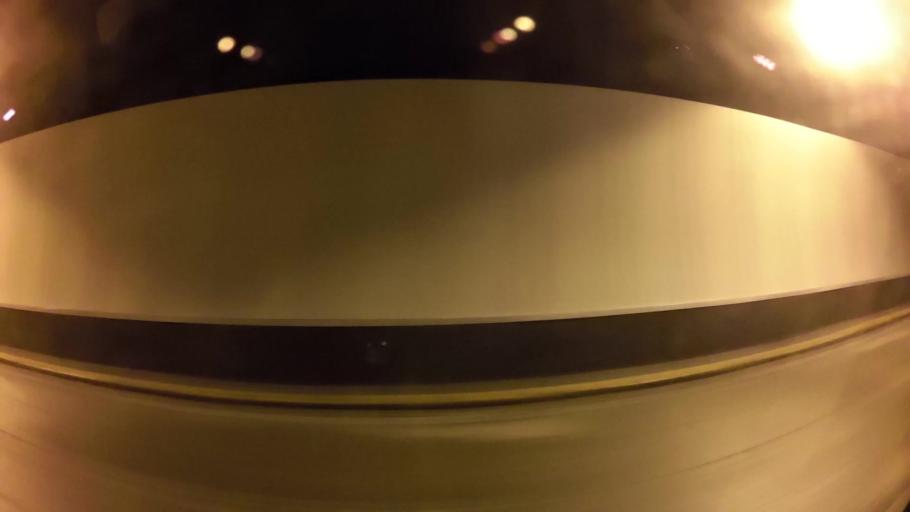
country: CL
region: Santiago Metropolitan
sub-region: Provincia de Santiago
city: Santiago
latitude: -33.4013
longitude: -70.6143
